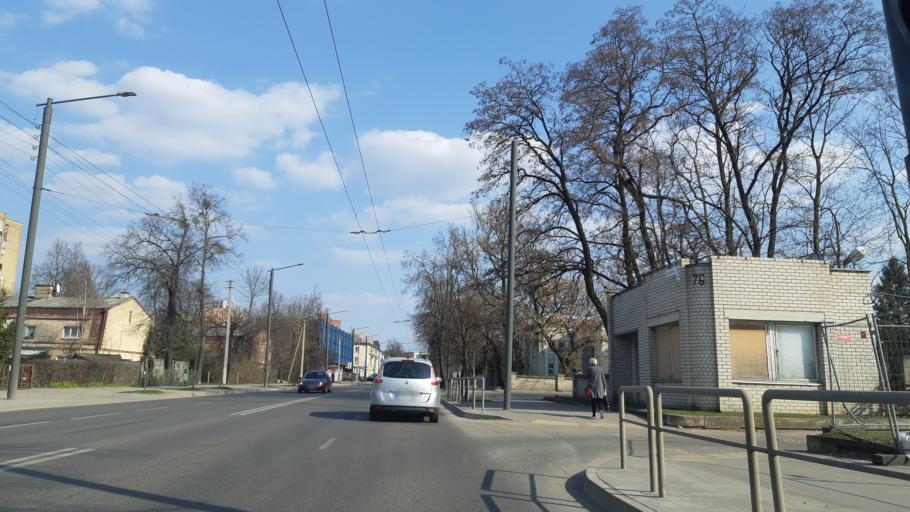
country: LT
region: Kauno apskritis
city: Dainava (Kaunas)
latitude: 54.8930
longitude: 23.9976
